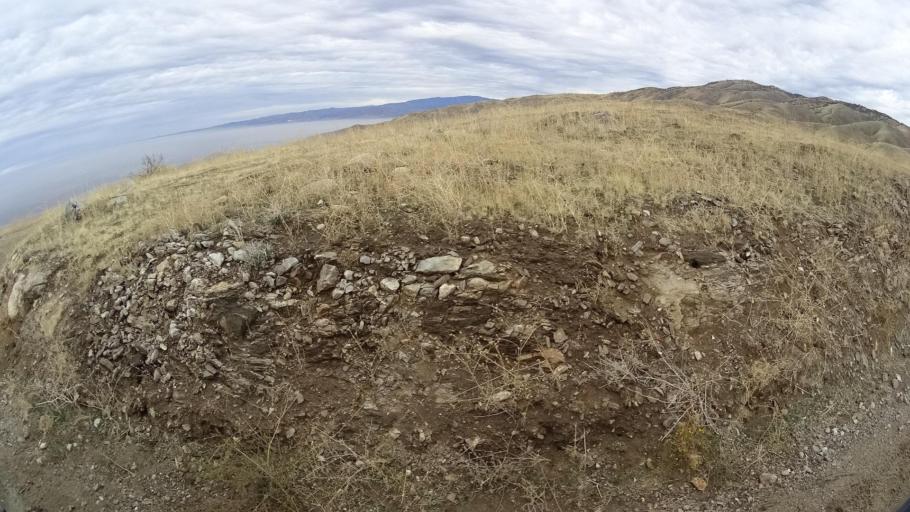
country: US
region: California
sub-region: Kern County
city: Arvin
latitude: 35.1376
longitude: -118.7825
